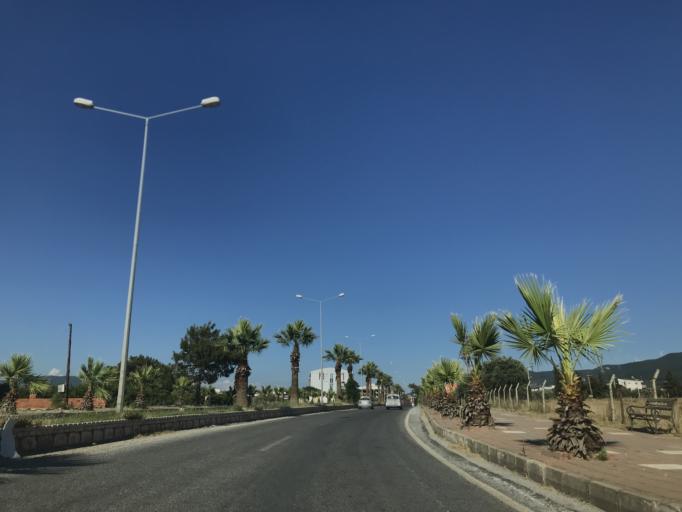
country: TR
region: Aydin
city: Davutlar
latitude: 37.7326
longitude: 27.2746
